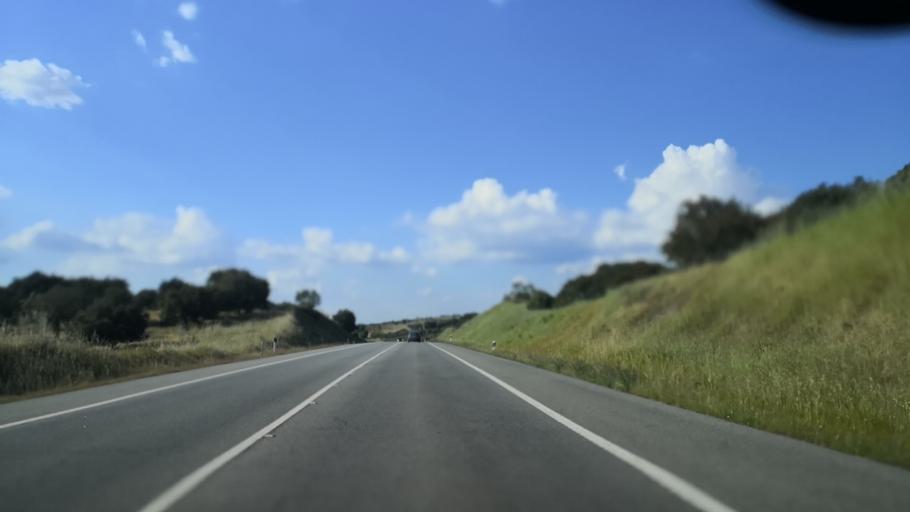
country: PT
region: Portalegre
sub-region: Arronches
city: Arronches
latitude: 39.0709
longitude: -7.4355
